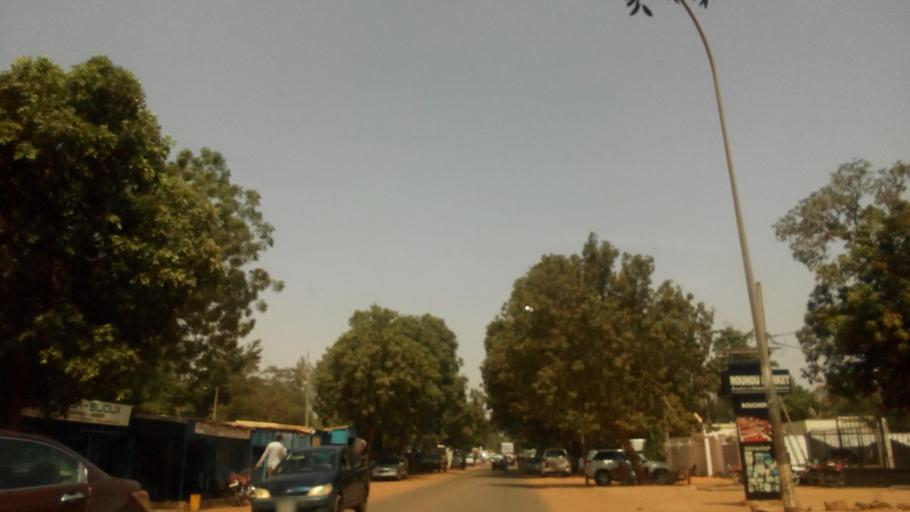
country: NE
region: Niamey
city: Niamey
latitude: 13.5222
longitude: 2.0961
